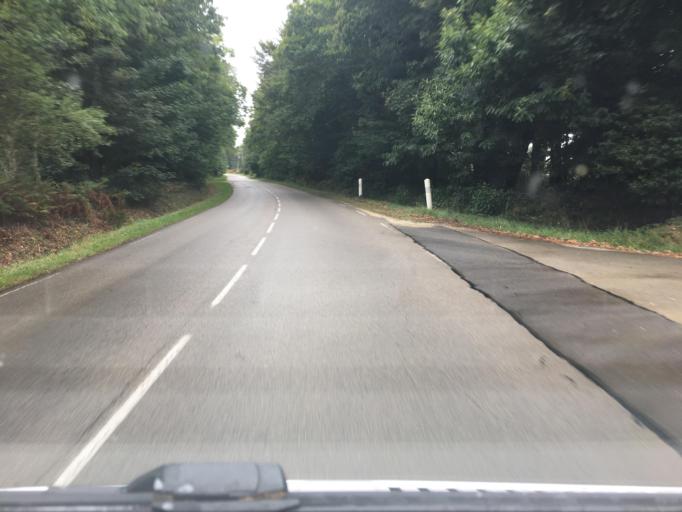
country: FR
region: Brittany
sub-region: Departement du Finistere
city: Poullan-sur-Mer
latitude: 48.0861
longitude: -4.3892
